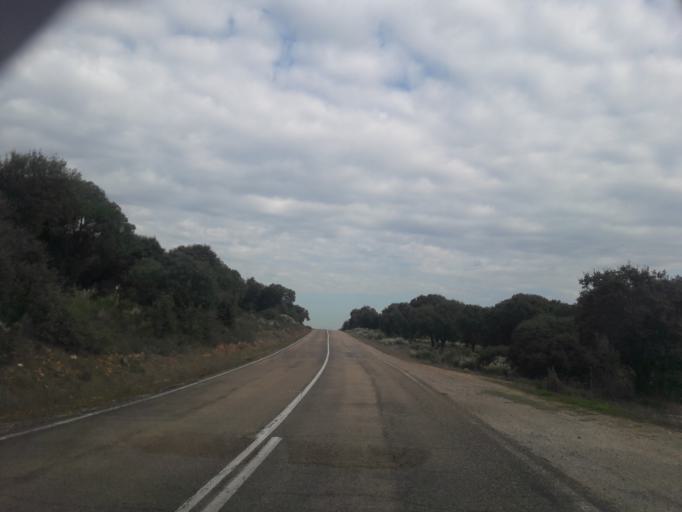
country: ES
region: Castille and Leon
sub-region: Provincia de Salamanca
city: Ciudad Rodrigo
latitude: 40.5634
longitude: -6.5276
